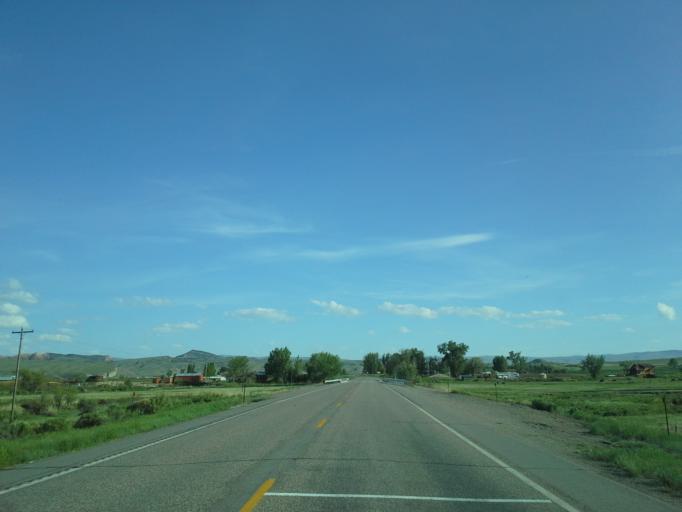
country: US
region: Wyoming
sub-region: Hot Springs County
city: Thermopolis
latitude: 43.7170
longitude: -108.1765
